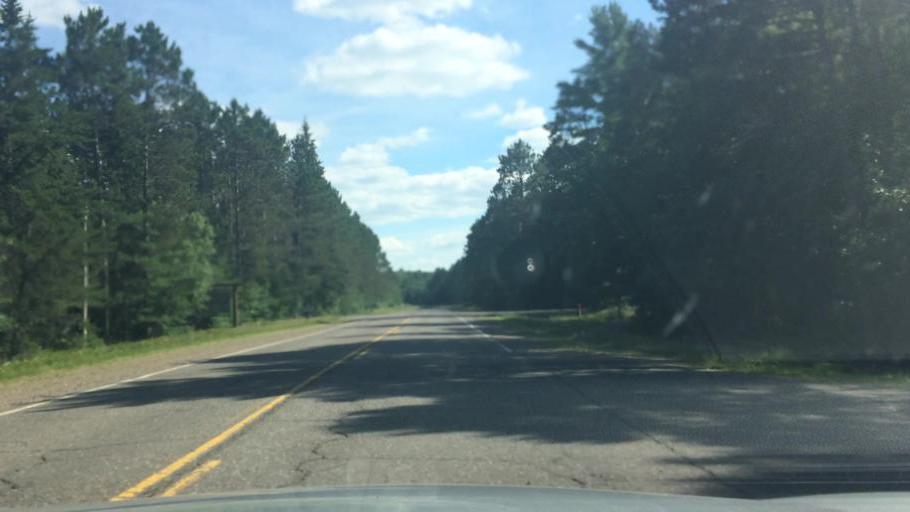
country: US
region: Wisconsin
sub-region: Vilas County
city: Lac du Flambeau
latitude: 46.0516
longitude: -89.6499
